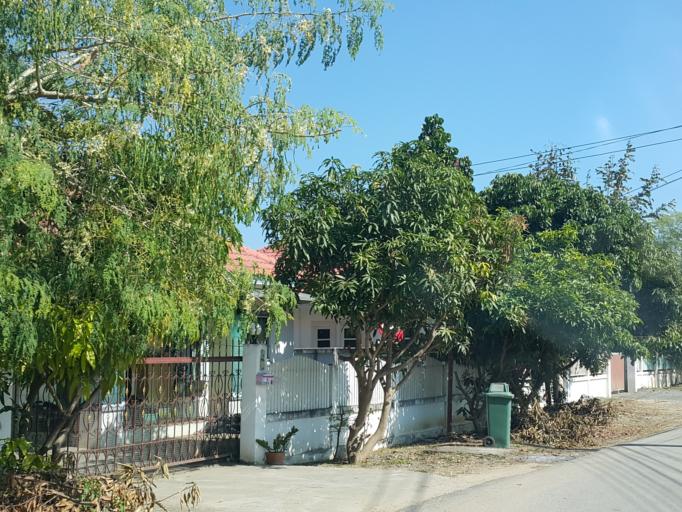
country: TH
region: Chiang Mai
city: San Sai
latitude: 18.8524
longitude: 98.9979
